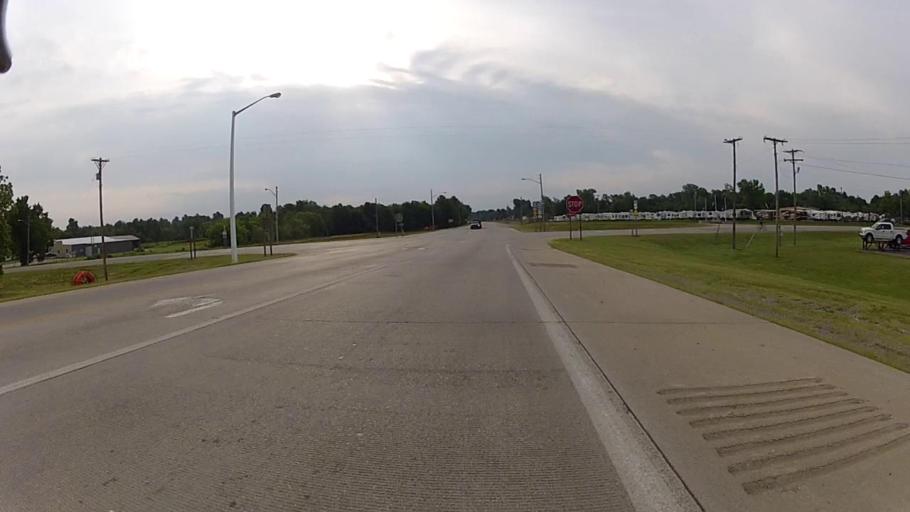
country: US
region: Kansas
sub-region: Cherokee County
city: Columbus
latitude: 37.1785
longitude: -94.8324
